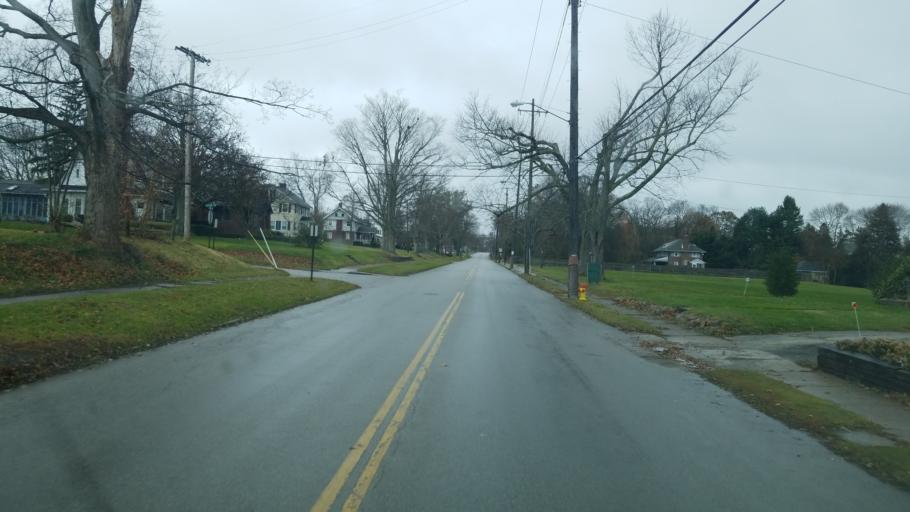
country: US
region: Ohio
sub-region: Ashtabula County
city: Ashtabula
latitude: 41.8500
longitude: -80.7950
